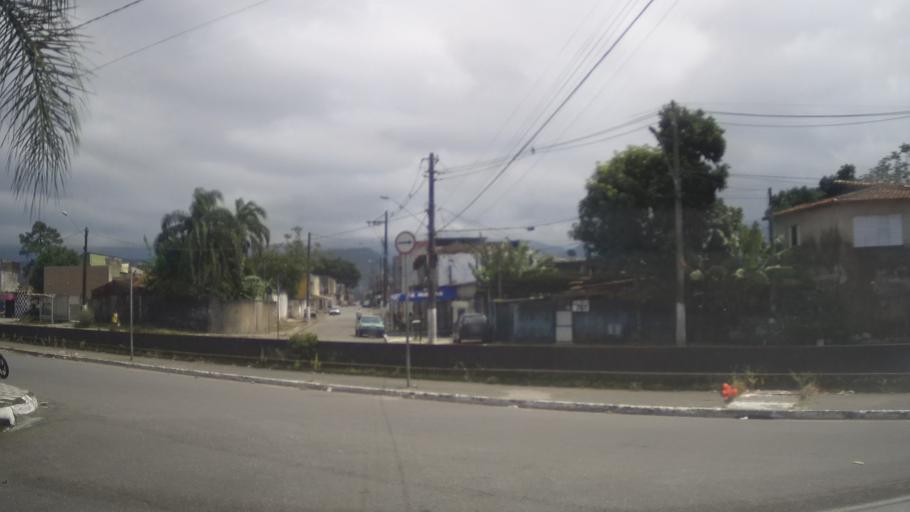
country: BR
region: Sao Paulo
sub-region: Praia Grande
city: Praia Grande
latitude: -24.0218
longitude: -46.4975
